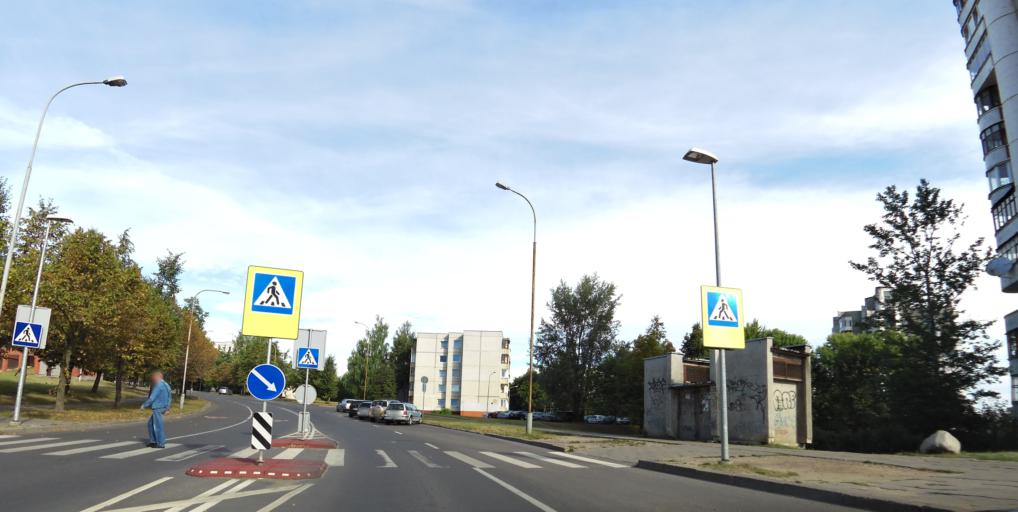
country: LT
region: Vilnius County
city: Seskine
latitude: 54.7161
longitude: 25.2510
